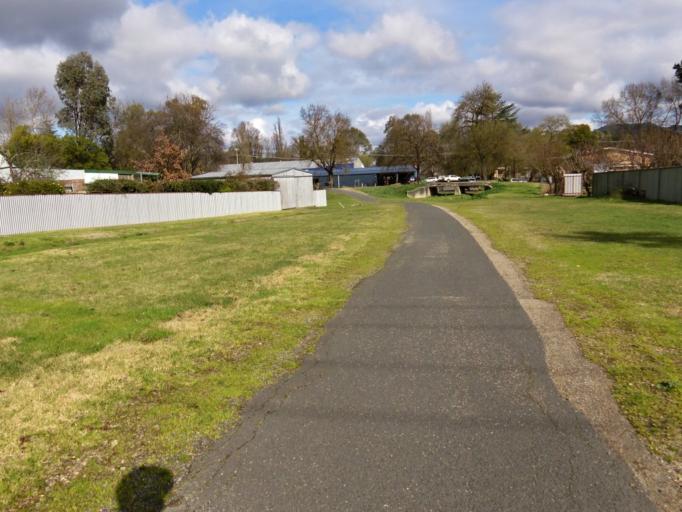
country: AU
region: Victoria
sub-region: Wangaratta
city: Wangaratta
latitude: -36.5644
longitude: 146.7301
